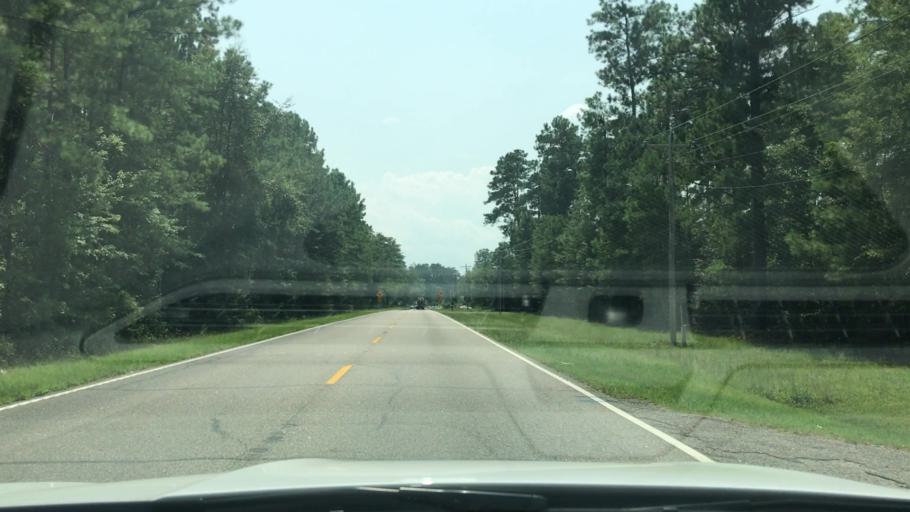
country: US
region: South Carolina
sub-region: Georgetown County
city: Georgetown
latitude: 33.4868
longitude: -79.2668
